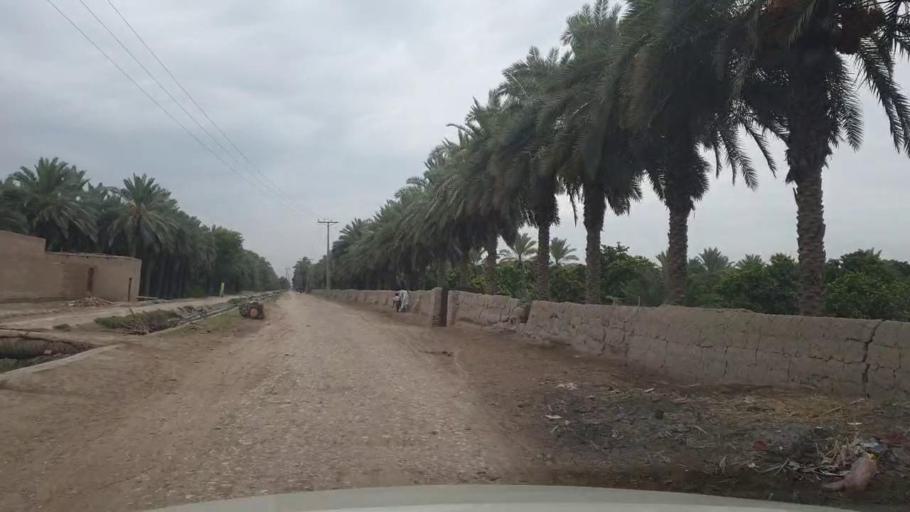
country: PK
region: Sindh
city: Sukkur
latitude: 27.6224
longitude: 68.8196
